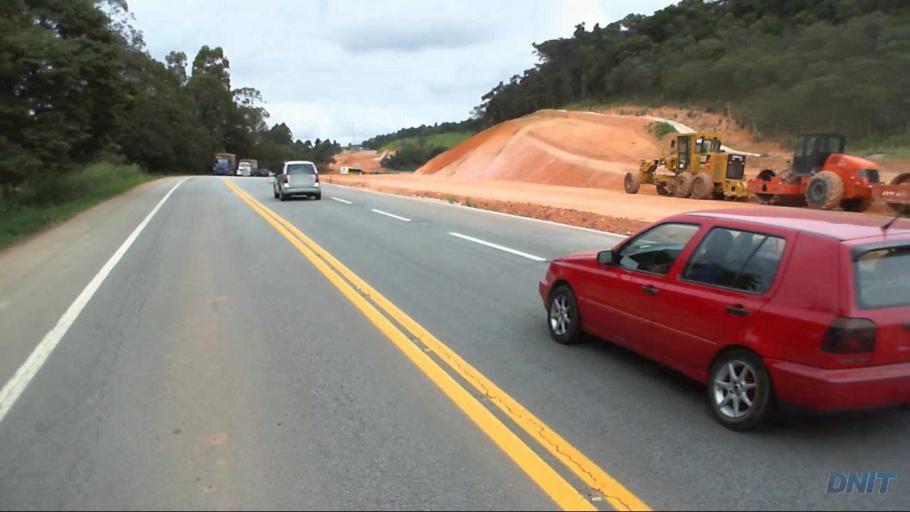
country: BR
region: Minas Gerais
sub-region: Caete
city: Caete
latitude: -19.7436
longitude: -43.5508
